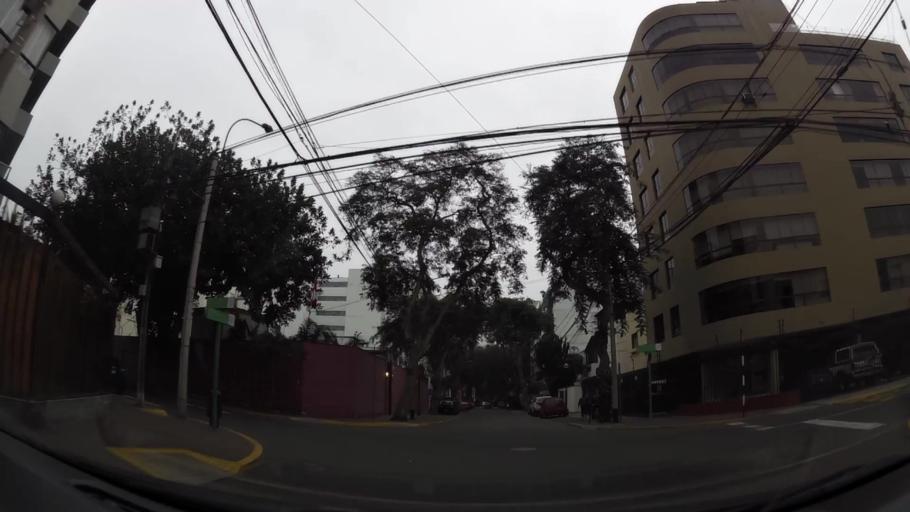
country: PE
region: Lima
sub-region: Lima
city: Surco
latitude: -12.1293
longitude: -77.0282
